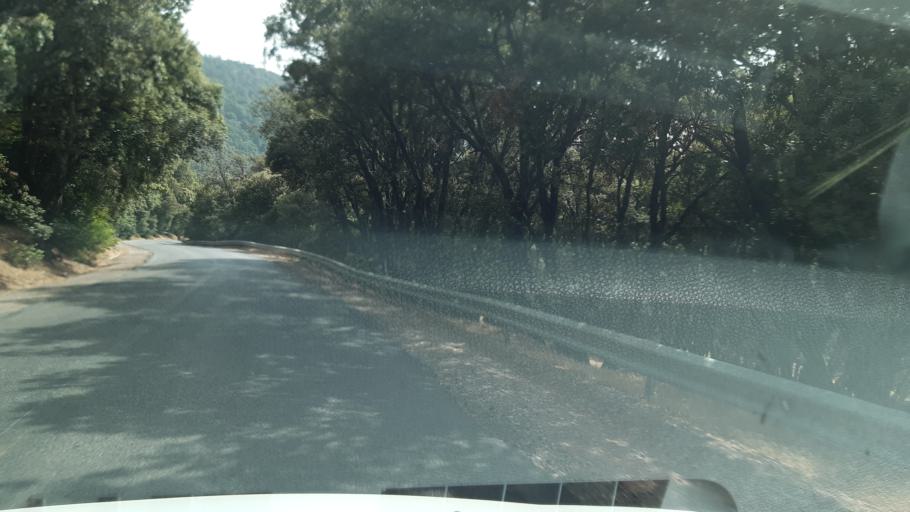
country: MA
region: Meknes-Tafilalet
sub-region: Ifrane
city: Azrou
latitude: 33.4300
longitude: -5.1893
